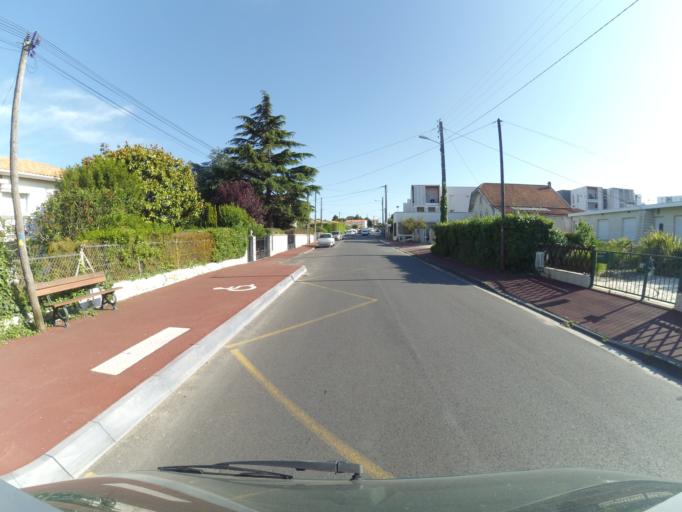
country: FR
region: Poitou-Charentes
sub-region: Departement de la Charente-Maritime
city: Royan
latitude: 45.6373
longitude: -1.0257
